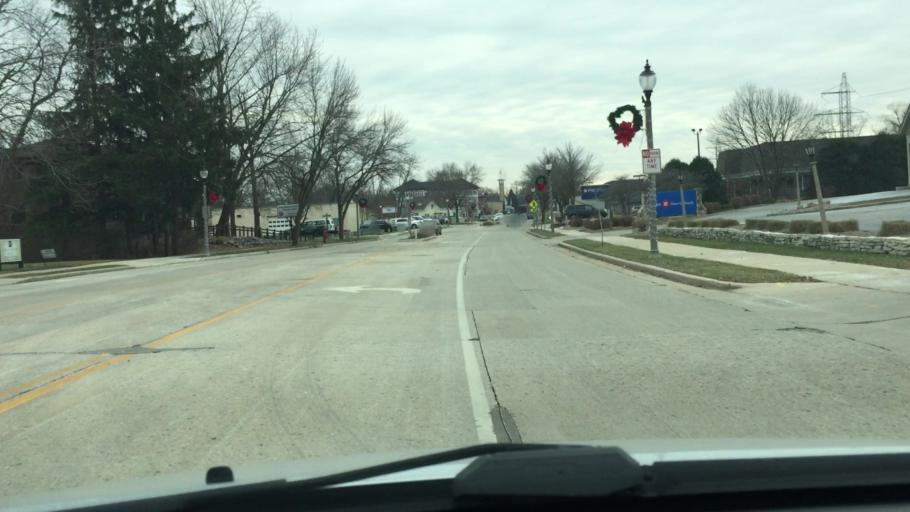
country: US
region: Wisconsin
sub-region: Ozaukee County
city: Mequon
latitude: 43.2344
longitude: -87.9839
